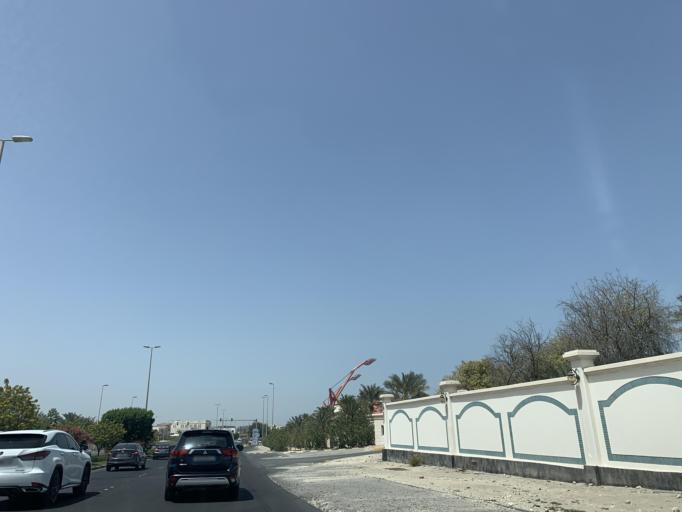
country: BH
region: Northern
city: Ar Rifa'
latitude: 26.1491
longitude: 50.5423
